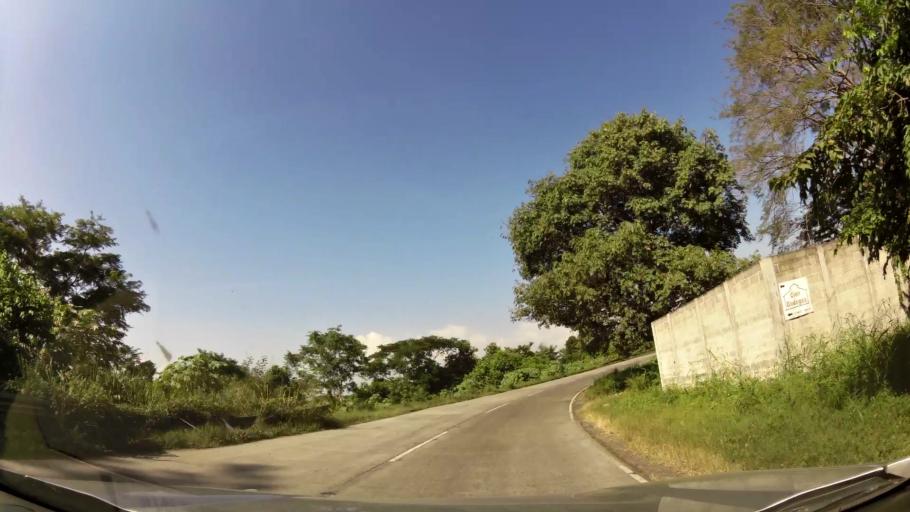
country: GT
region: Escuintla
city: Puerto San Jose
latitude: 13.9389
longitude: -90.7906
